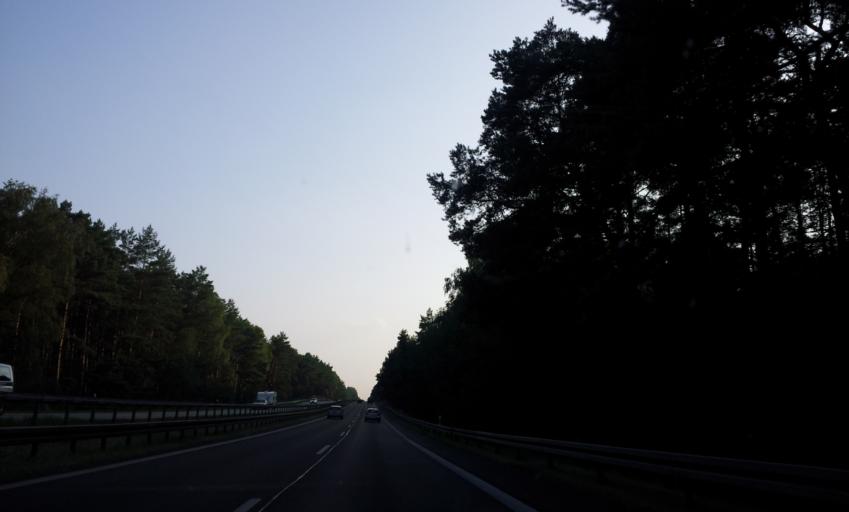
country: DE
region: Brandenburg
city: Marienwerder
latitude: 52.7931
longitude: 13.5945
